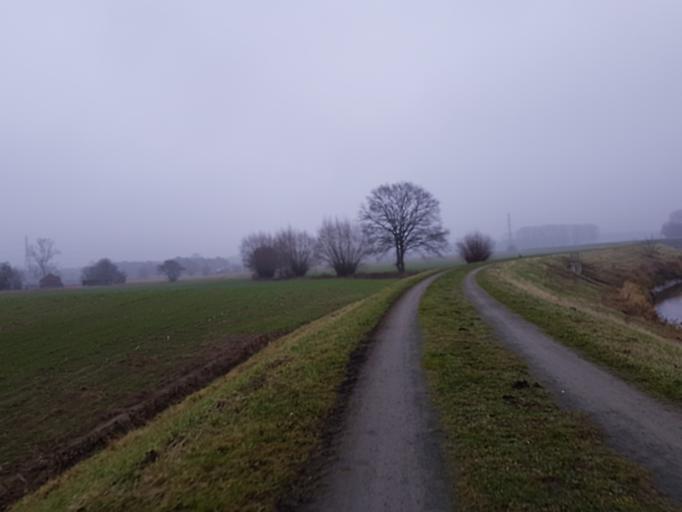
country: BE
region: Flanders
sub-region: Provincie Vlaams-Brabant
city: Keerbergen
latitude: 50.9936
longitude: 4.6191
